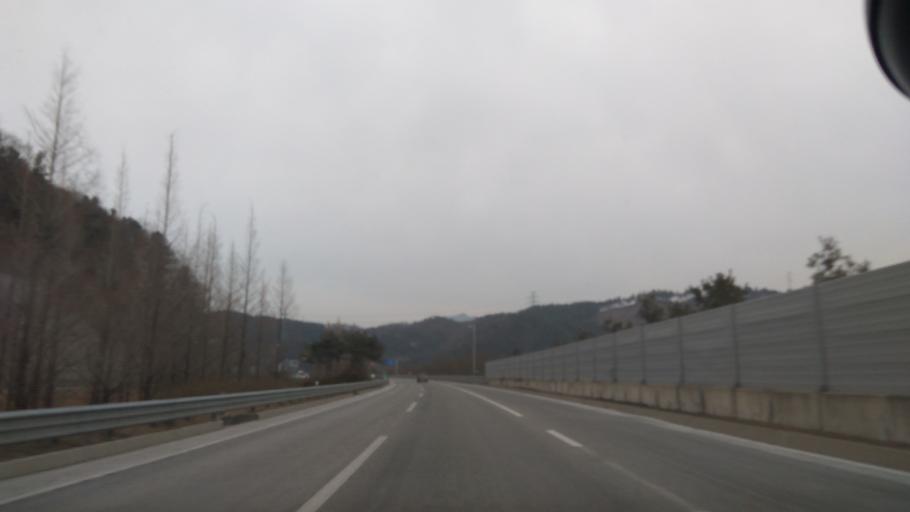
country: KR
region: Gyeonggi-do
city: Cheongpyeong
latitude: 37.6526
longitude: 127.4840
